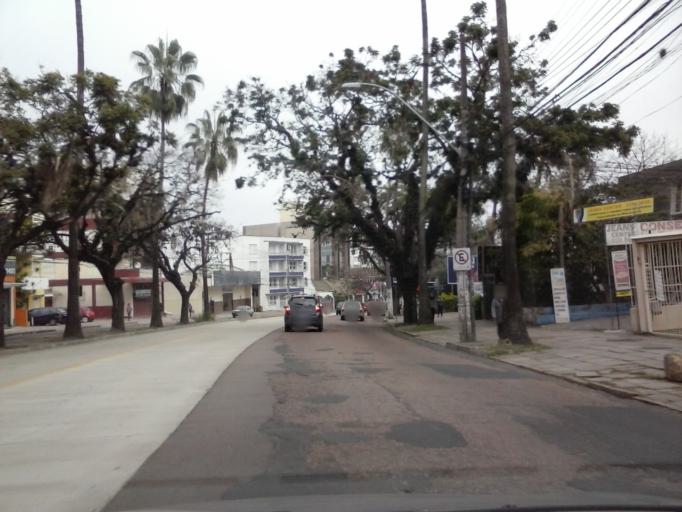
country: BR
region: Rio Grande do Sul
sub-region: Porto Alegre
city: Porto Alegre
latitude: -30.0413
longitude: -51.1778
